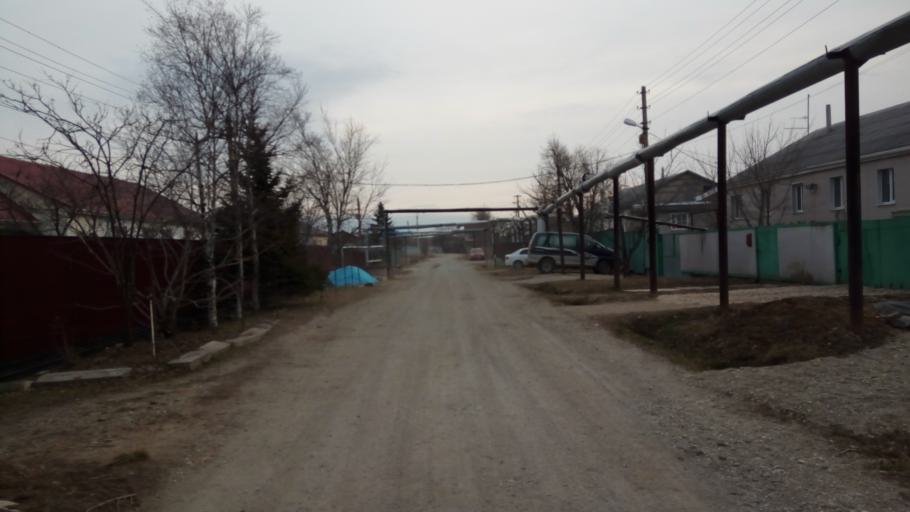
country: RU
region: Primorskiy
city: Novoshakhtinskiy
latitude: 44.0248
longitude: 132.1775
